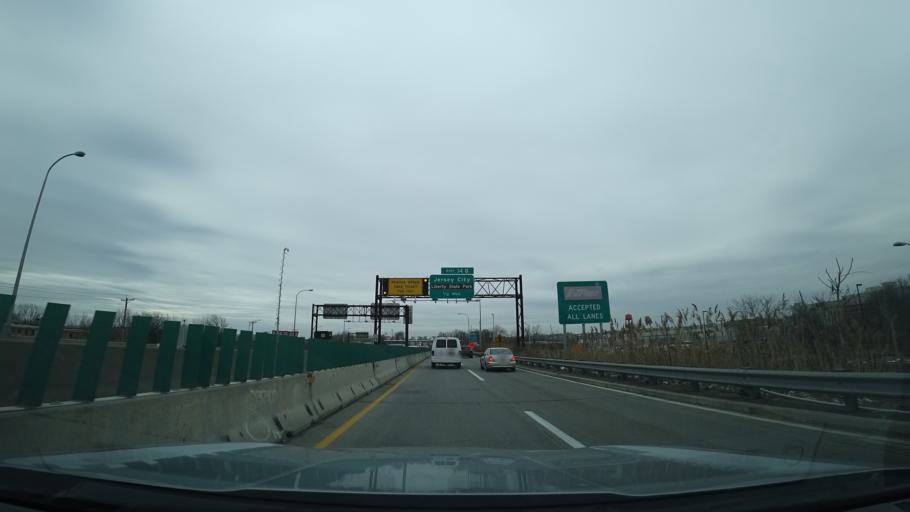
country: US
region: New Jersey
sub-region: Hudson County
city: Jersey City
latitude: 40.7079
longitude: -74.0591
